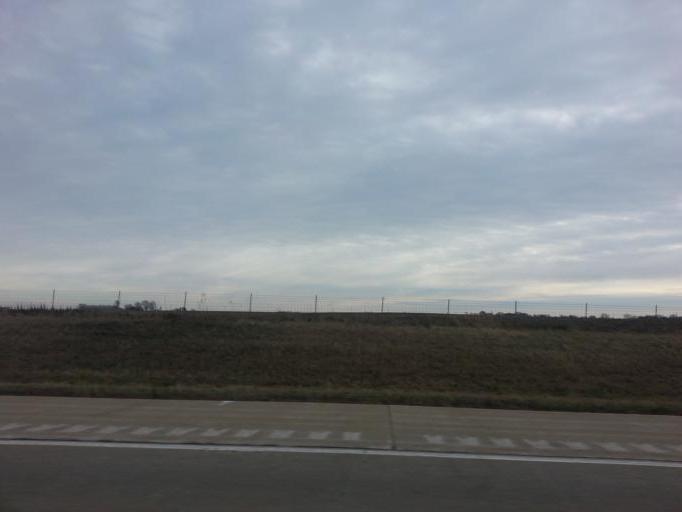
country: US
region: Illinois
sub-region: Woodford County
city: El Paso
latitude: 40.7678
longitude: -89.0345
